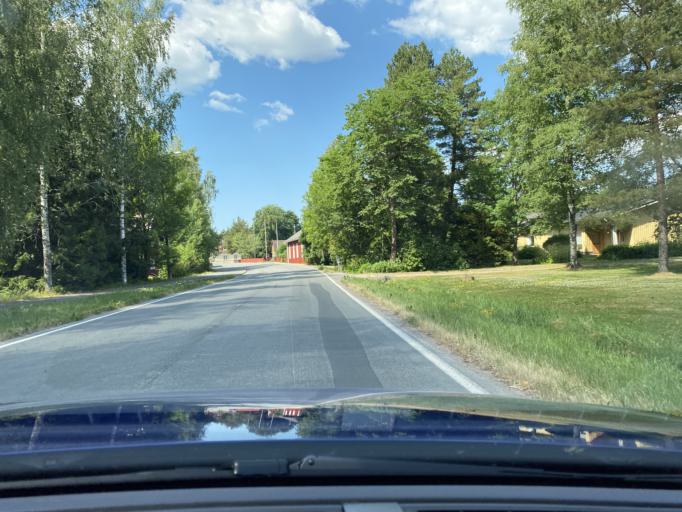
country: FI
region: Satakunta
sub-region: Rauma
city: Eura
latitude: 61.1401
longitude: 22.1227
